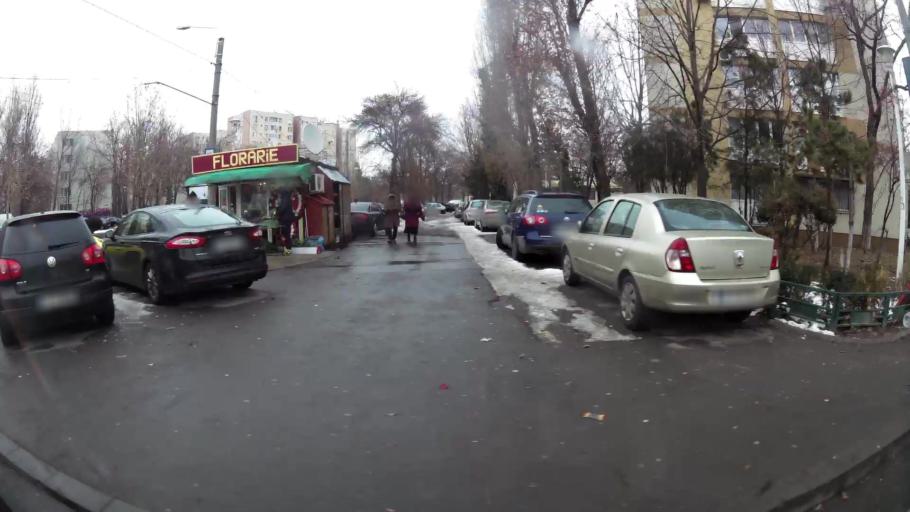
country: RO
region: Ilfov
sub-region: Comuna Chiajna
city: Rosu
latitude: 44.4175
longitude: 26.0281
